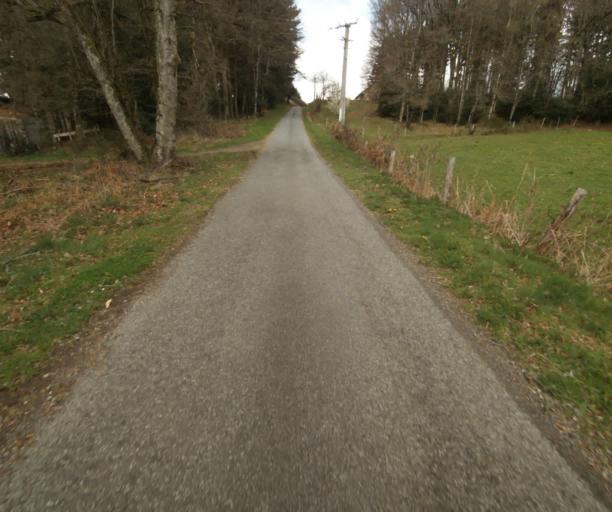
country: FR
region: Limousin
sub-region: Departement de la Correze
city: Correze
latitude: 45.3504
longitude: 1.9349
